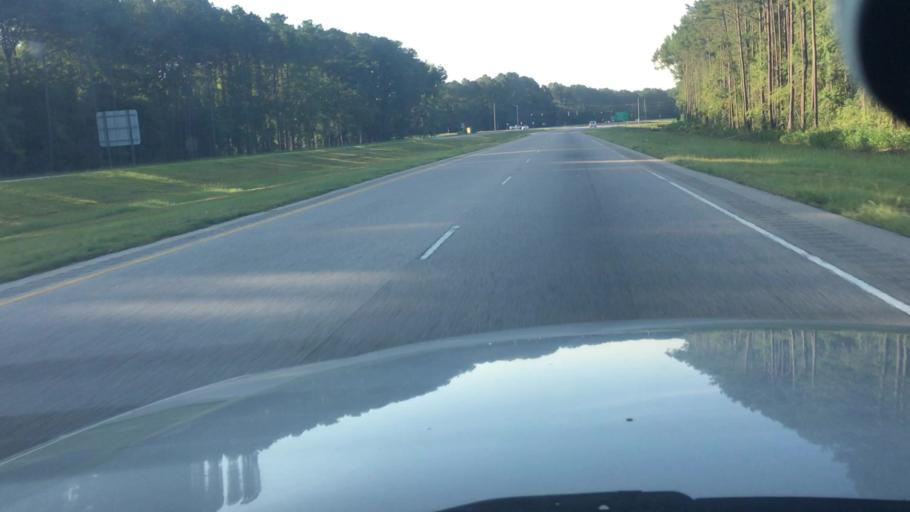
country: US
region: North Carolina
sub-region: Cumberland County
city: Vander
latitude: 34.9639
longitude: -78.8476
